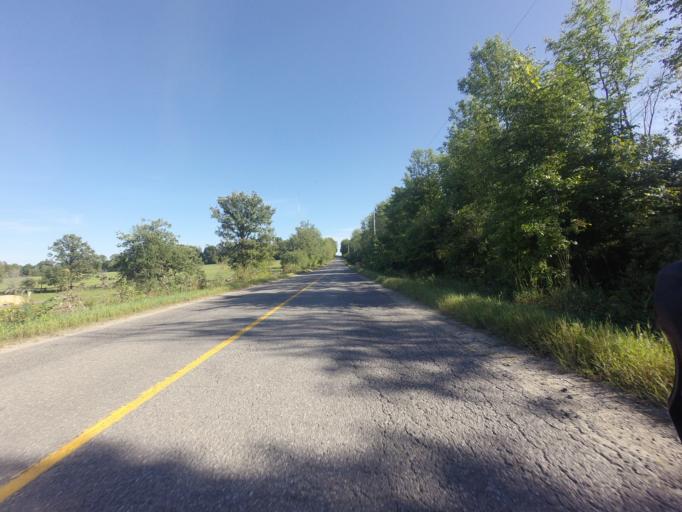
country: CA
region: Ontario
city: Perth
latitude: 44.9250
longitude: -76.3622
